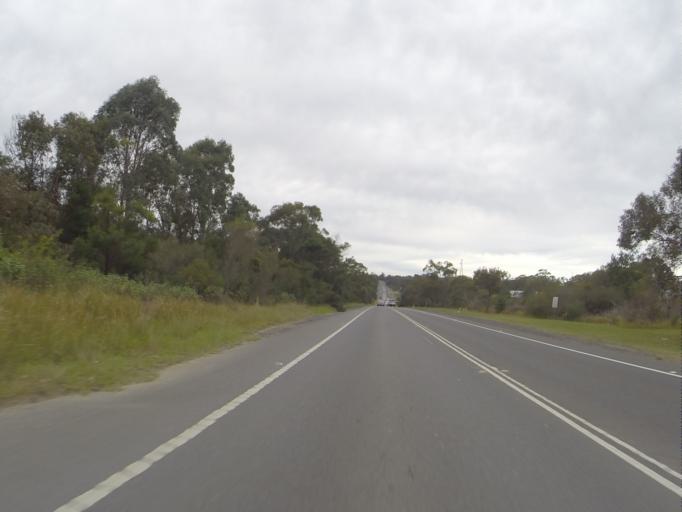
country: AU
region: New South Wales
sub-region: Sutherland Shire
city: Engadine
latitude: -34.0473
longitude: 150.9840
